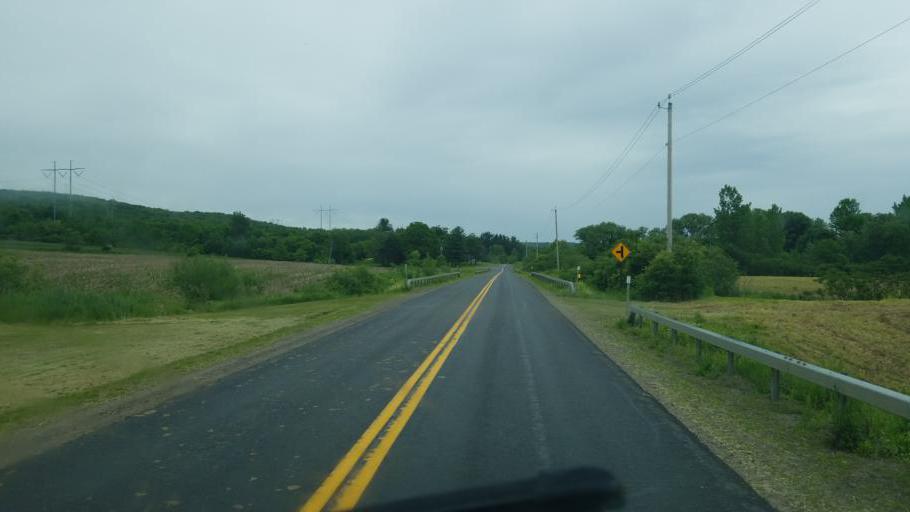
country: US
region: New York
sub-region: Herkimer County
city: Frankfort
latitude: 43.0861
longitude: -75.0800
